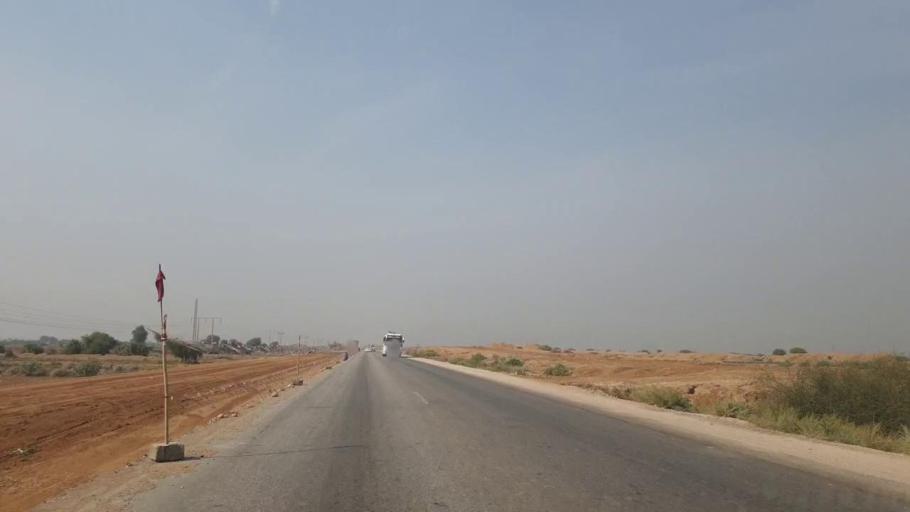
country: PK
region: Sindh
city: Sann
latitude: 26.1235
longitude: 68.0567
